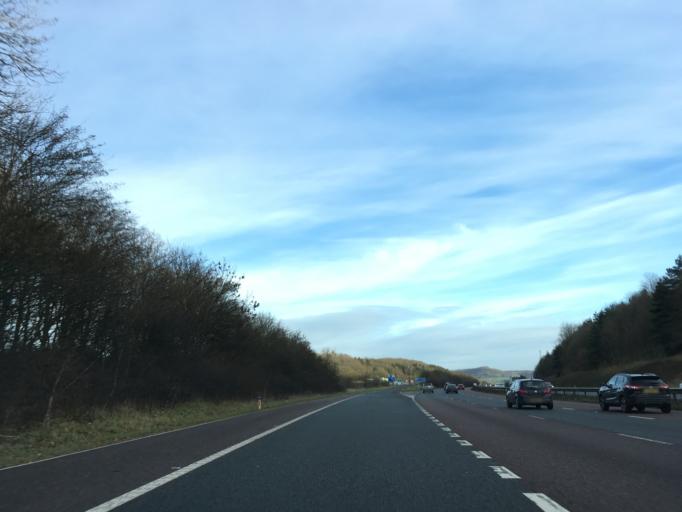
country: GB
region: England
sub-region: South Gloucestershire
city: Falfield
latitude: 51.6531
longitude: -2.4368
